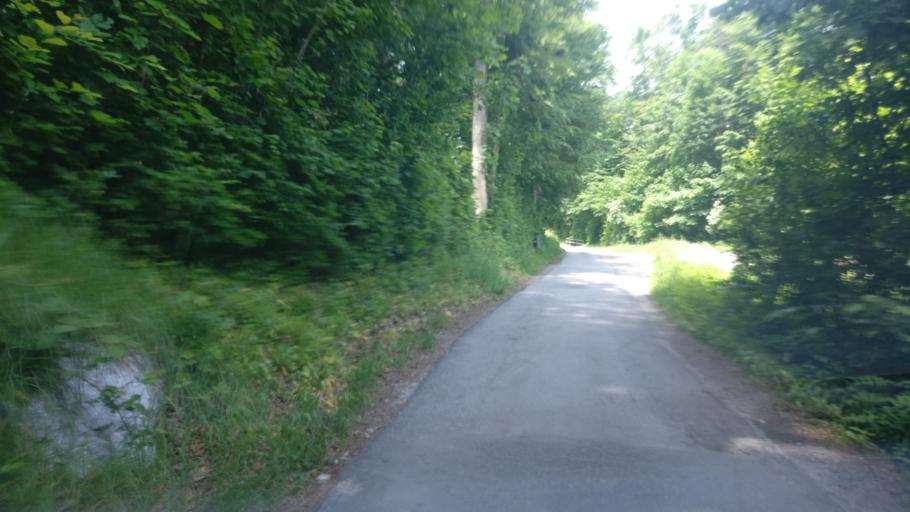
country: AT
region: Salzburg
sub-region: Politischer Bezirk Hallein
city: Hallein
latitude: 47.6588
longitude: 13.1149
